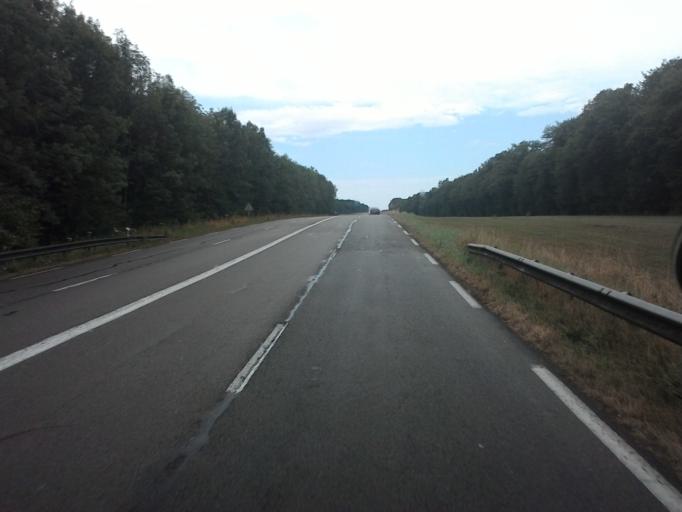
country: FR
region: Franche-Comte
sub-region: Departement du Jura
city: Poligny
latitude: 46.8379
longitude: 5.6173
